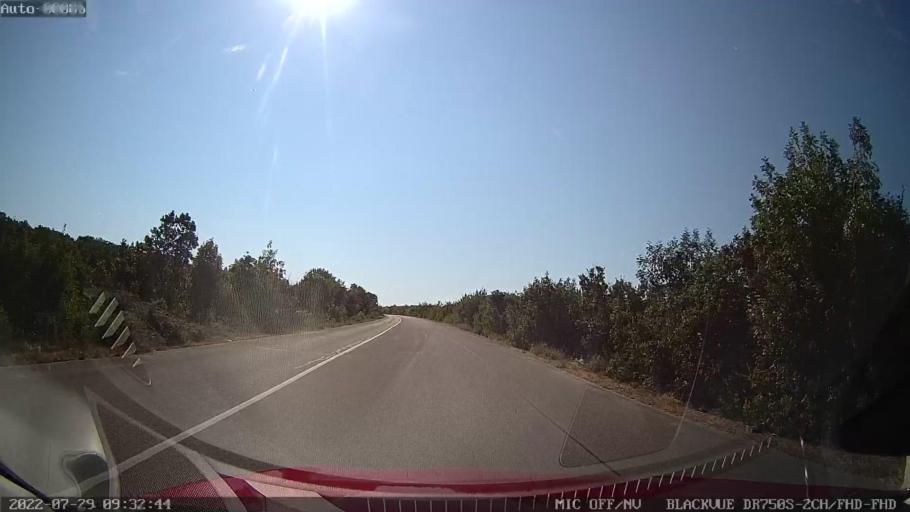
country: HR
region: Zadarska
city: Obrovac
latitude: 44.1815
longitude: 15.7157
